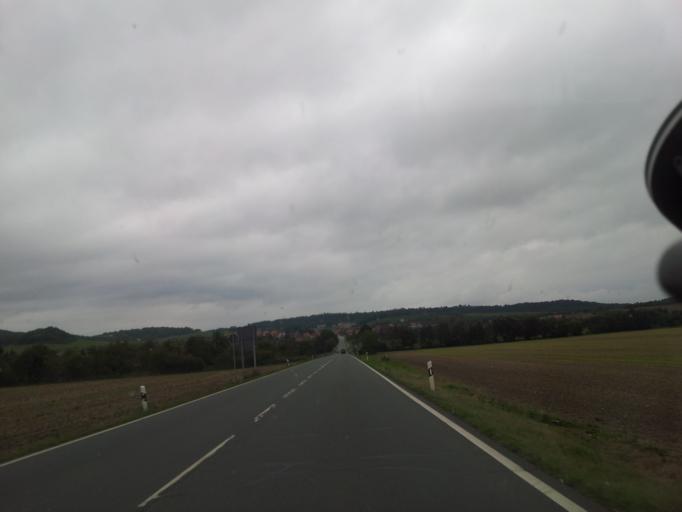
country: DE
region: Saxony-Anhalt
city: Blankenburg
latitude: 51.7643
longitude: 10.9617
